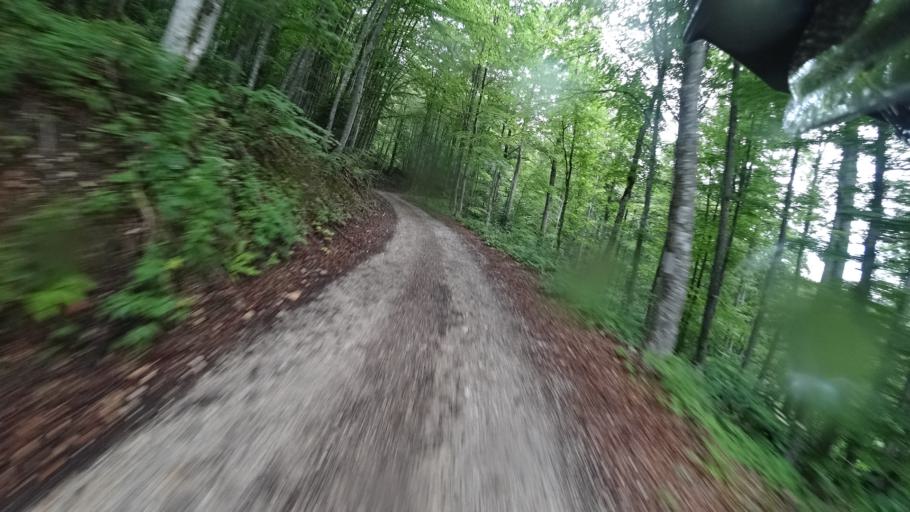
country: HR
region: Primorsko-Goranska
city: Vrbovsko
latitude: 45.3008
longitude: 14.9329
